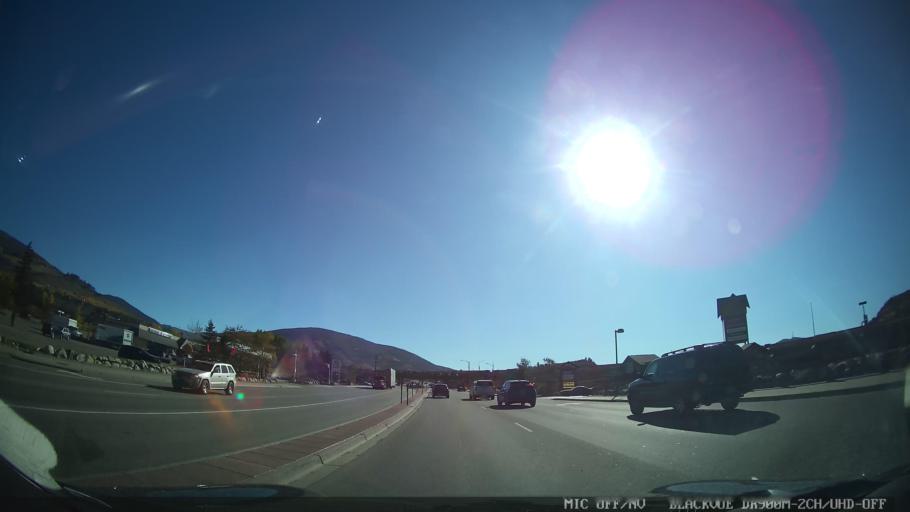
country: US
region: Colorado
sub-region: Summit County
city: Silverthorne
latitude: 39.6473
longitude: -106.0929
